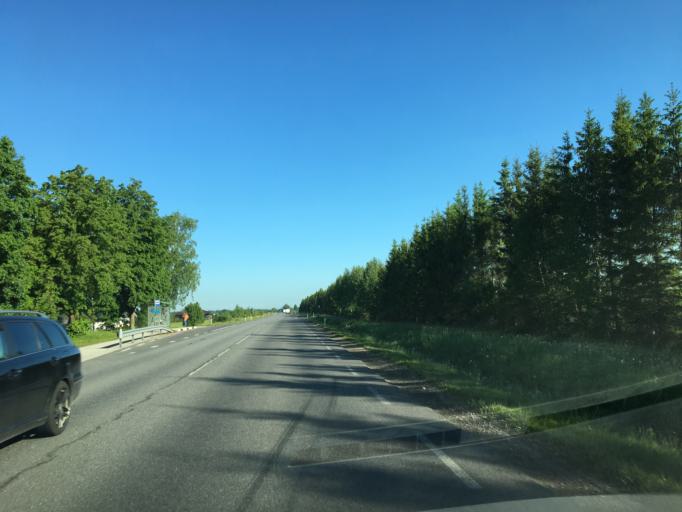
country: EE
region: Tartu
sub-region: Tartu linn
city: Tartu
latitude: 58.4210
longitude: 26.6987
